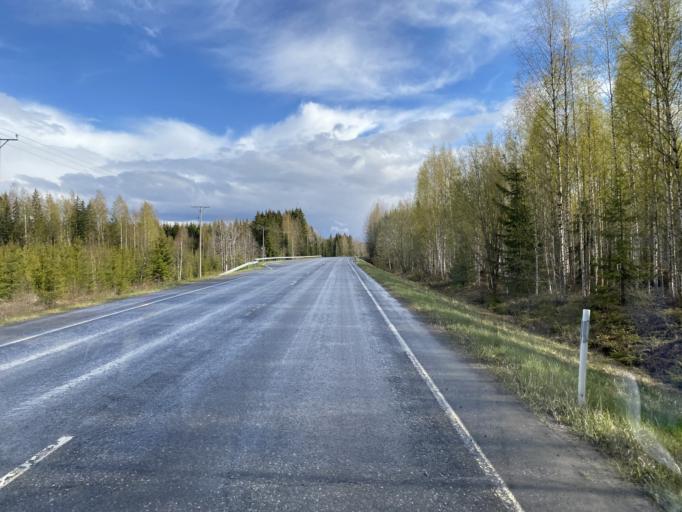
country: FI
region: Pirkanmaa
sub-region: Etelae-Pirkanmaa
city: Viiala
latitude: 61.2371
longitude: 23.7402
